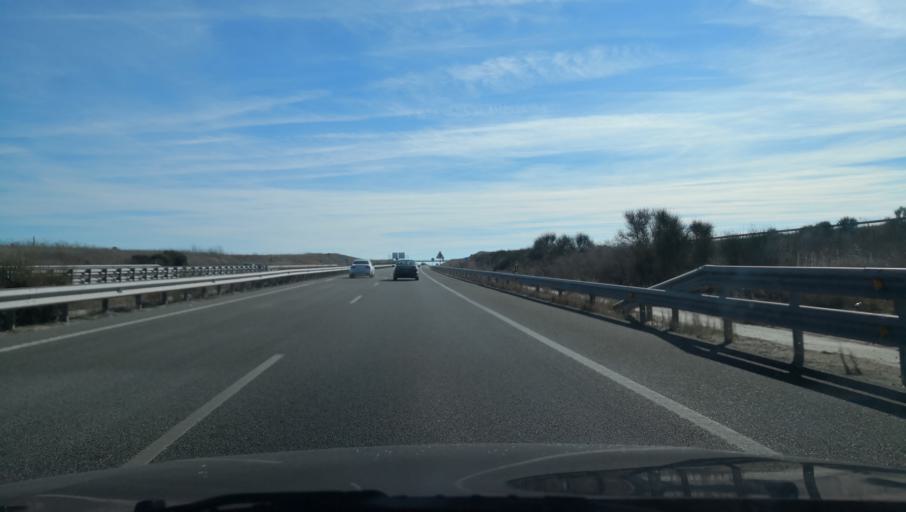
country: ES
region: Castille and Leon
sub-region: Provincia de Salamanca
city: Penaranda de Bracamonte
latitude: 40.9143
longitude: -5.1919
